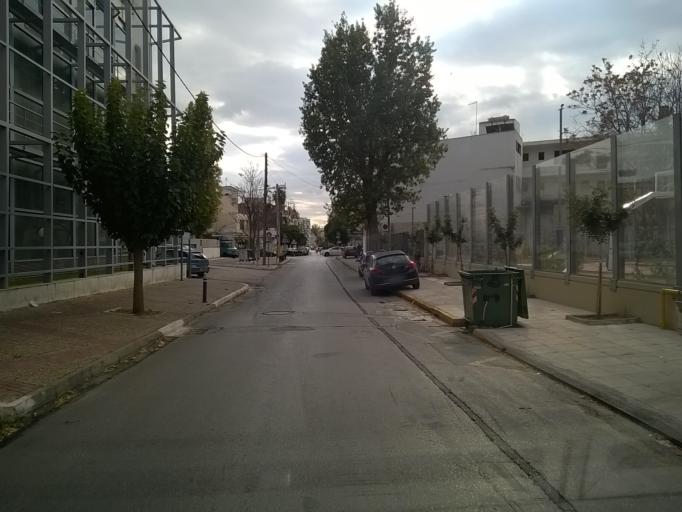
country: GR
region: Attica
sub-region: Nomos Piraios
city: Agios Ioannis Rentis
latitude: 37.9487
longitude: 23.6580
